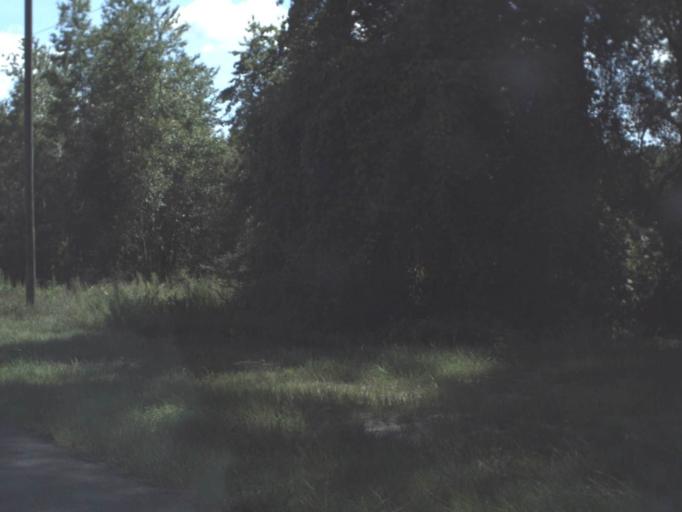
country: US
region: Florida
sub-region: Lafayette County
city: Mayo
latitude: 30.0663
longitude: -83.1747
